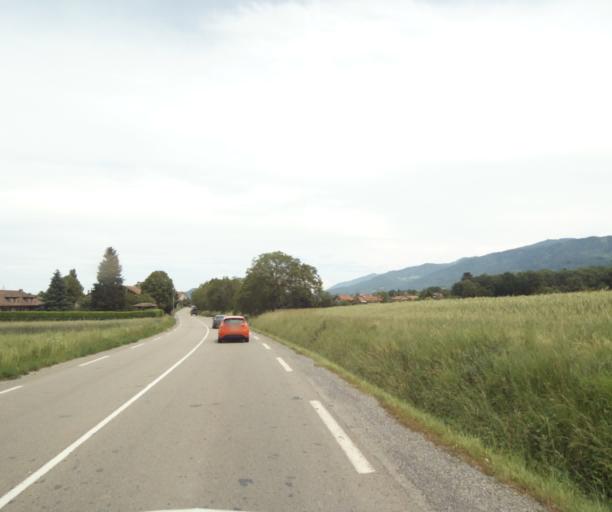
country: FR
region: Rhone-Alpes
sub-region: Departement de la Haute-Savoie
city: Bons-en-Chablais
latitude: 46.2745
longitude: 6.3965
